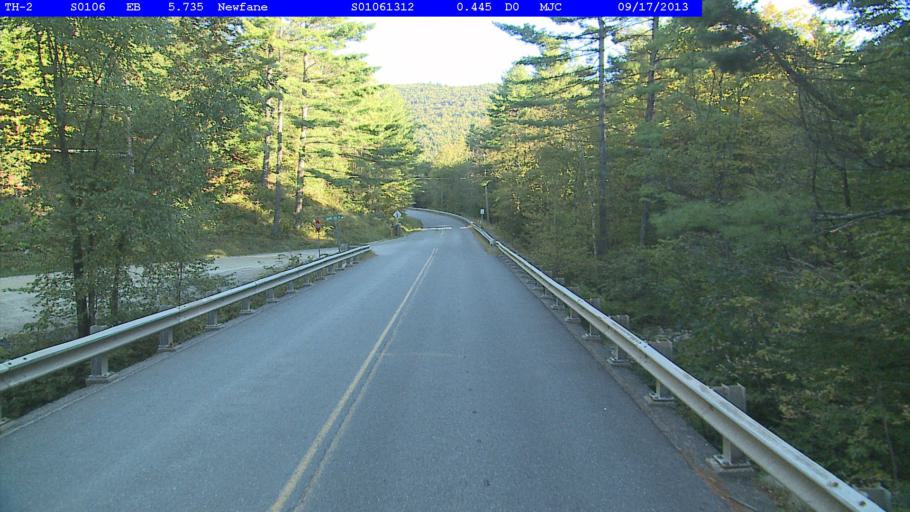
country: US
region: Vermont
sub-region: Windham County
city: Dover
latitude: 42.9488
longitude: -72.7577
